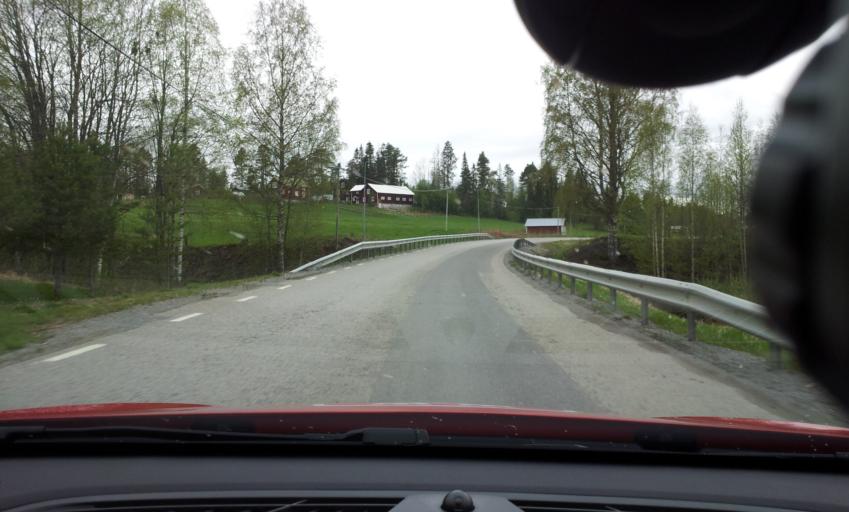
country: SE
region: Jaemtland
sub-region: Bergs Kommun
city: Hoverberg
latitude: 62.7758
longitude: 14.5195
